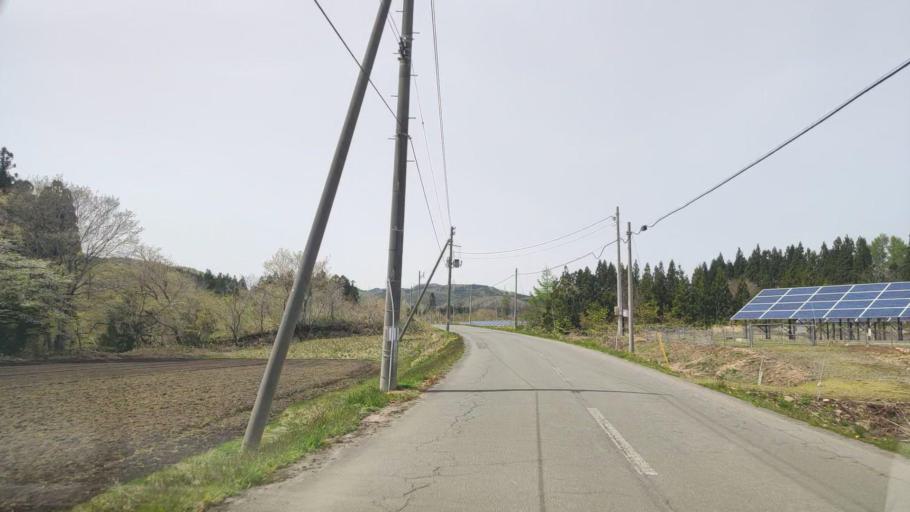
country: JP
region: Aomori
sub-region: Misawa Shi
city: Inuotose
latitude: 40.7836
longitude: 141.1163
